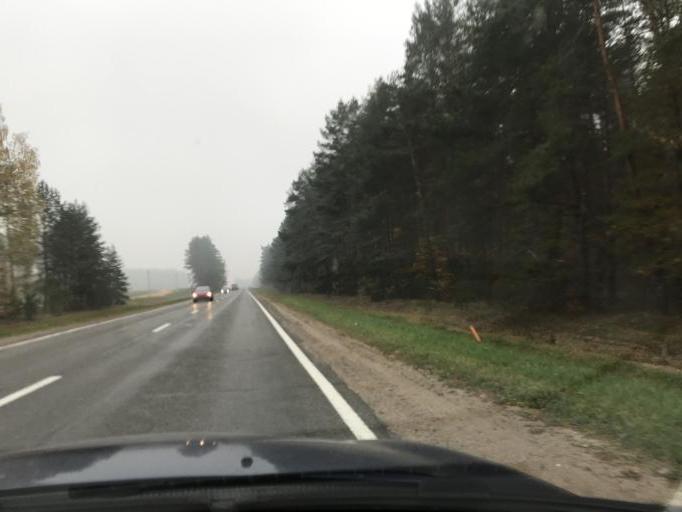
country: BY
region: Grodnenskaya
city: Hrodna
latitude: 53.7920
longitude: 23.8544
